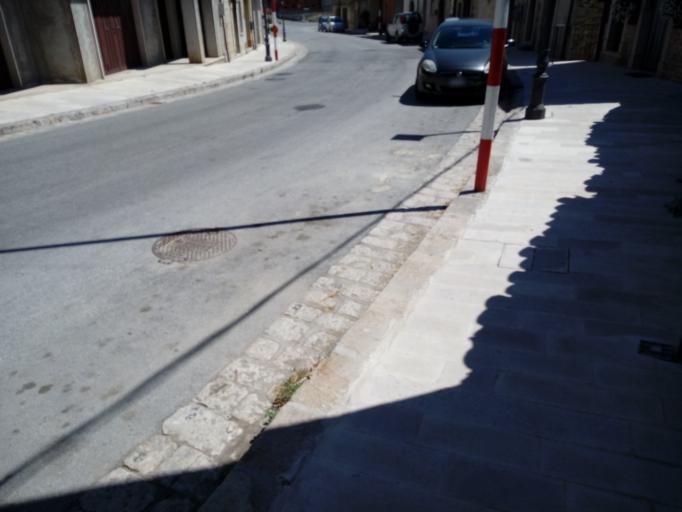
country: IT
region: Molise
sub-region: Provincia di Campobasso
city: Jelsi
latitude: 41.5184
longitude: 14.7953
